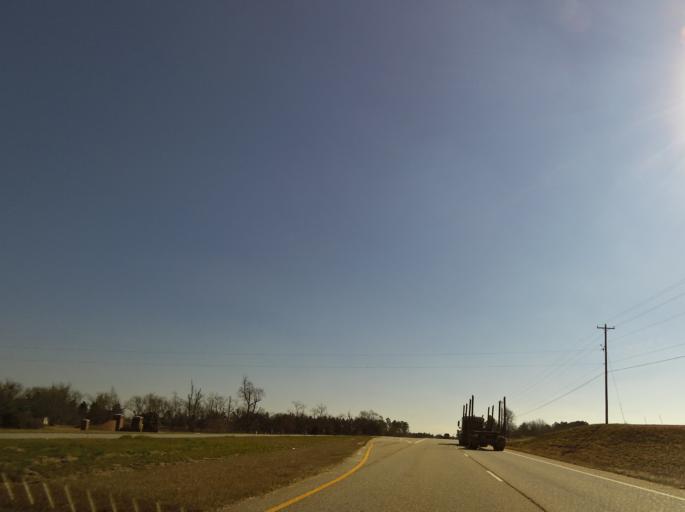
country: US
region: Georgia
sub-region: Pulaski County
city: Hawkinsville
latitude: 32.3106
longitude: -83.5144
